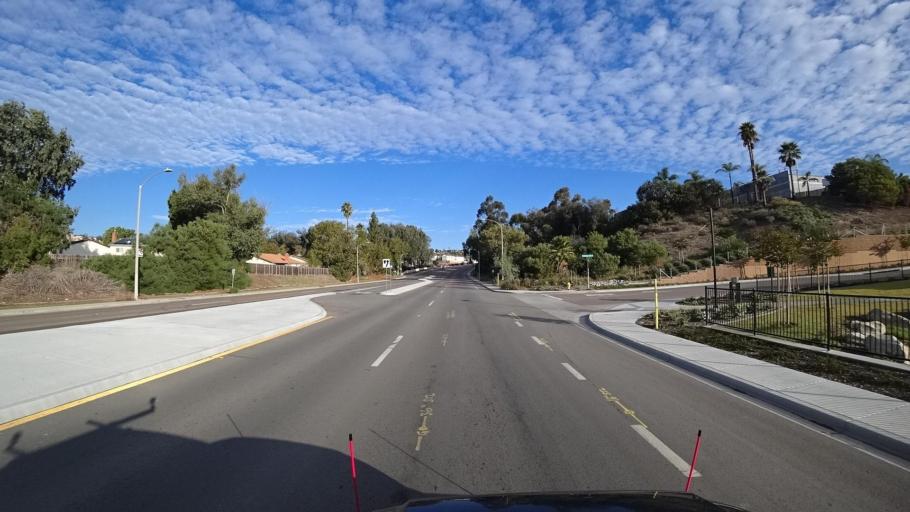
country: US
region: California
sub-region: San Diego County
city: La Presa
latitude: 32.7269
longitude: -116.9700
